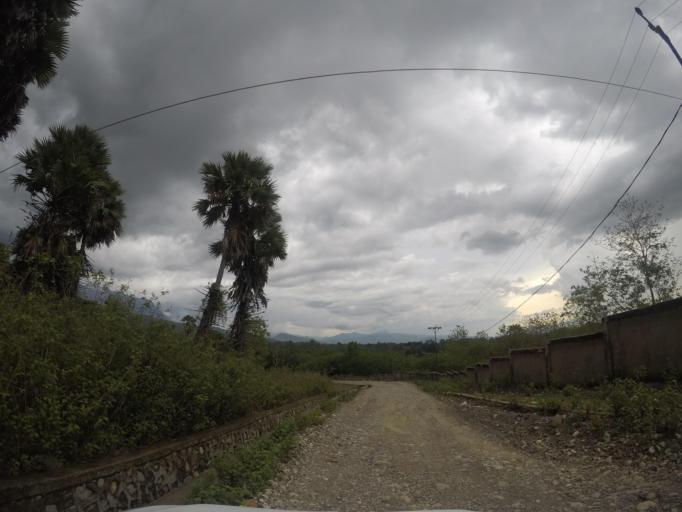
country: TL
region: Bobonaro
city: Maliana
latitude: -8.9731
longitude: 125.2264
